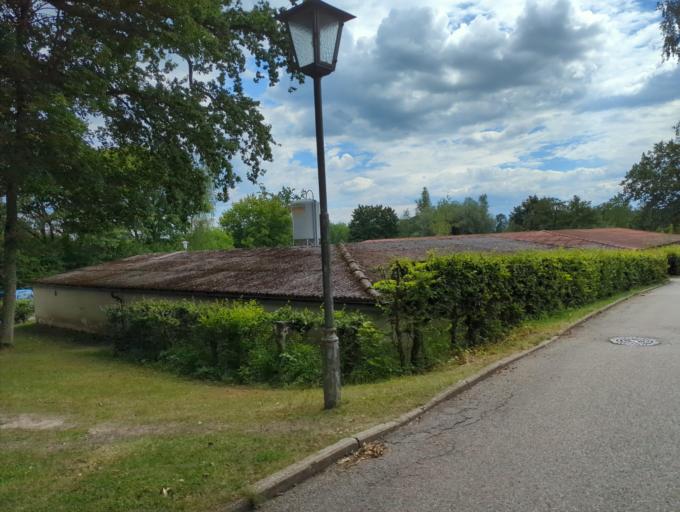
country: DE
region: Bavaria
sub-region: Upper Bavaria
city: Wasserburg am Inn
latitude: 48.0584
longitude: 12.2037
